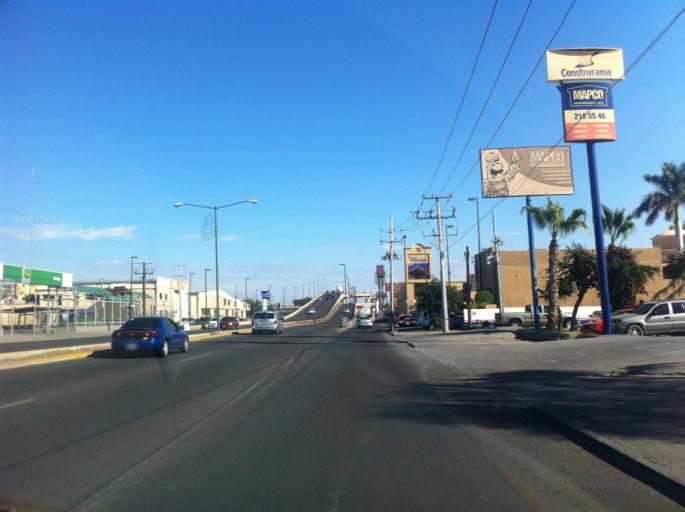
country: MX
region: Sonora
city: Hermosillo
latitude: 29.0941
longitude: -110.9987
